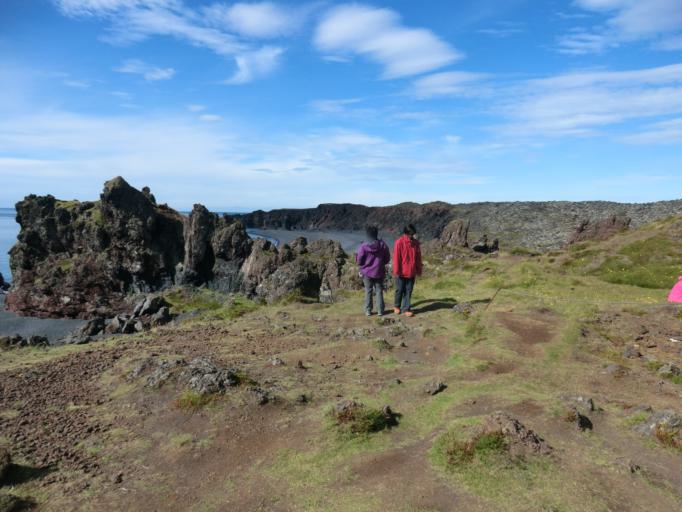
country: IS
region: West
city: Olafsvik
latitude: 64.7521
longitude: -23.8980
